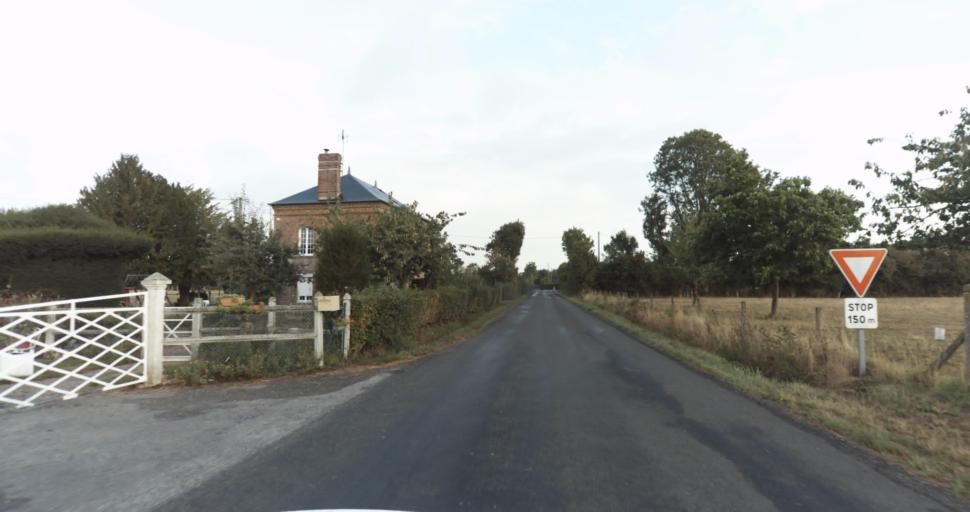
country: FR
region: Lower Normandy
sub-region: Departement de l'Orne
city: Vimoutiers
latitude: 48.9337
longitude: 0.2249
